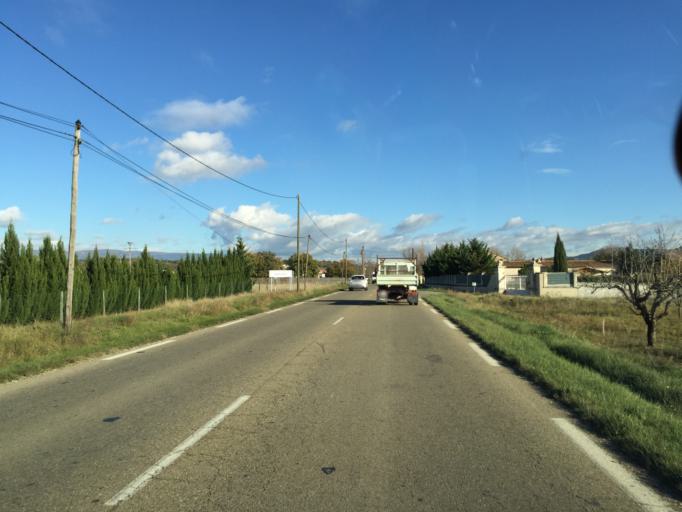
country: FR
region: Provence-Alpes-Cote d'Azur
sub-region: Departement du Vaucluse
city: Roussillon
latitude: 43.8639
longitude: 5.2980
